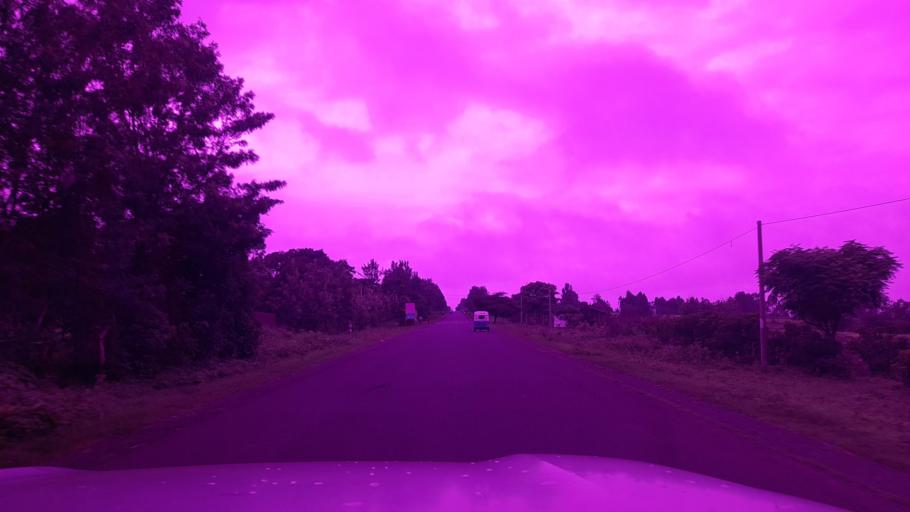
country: ET
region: Oromiya
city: Waliso
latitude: 8.2658
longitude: 37.6553
